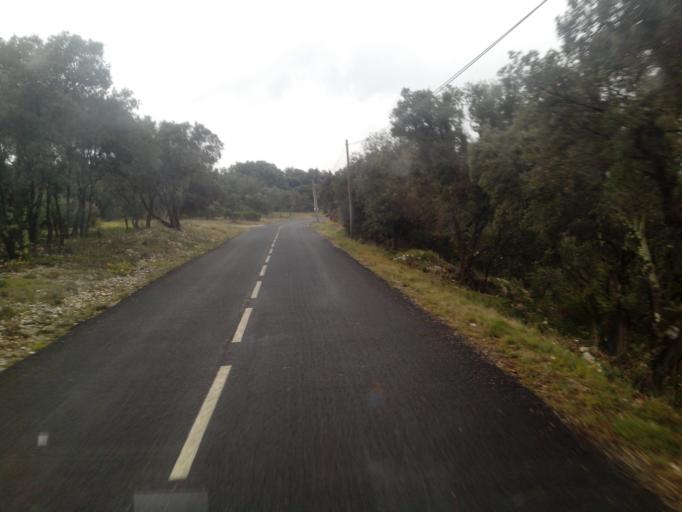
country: FR
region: Languedoc-Roussillon
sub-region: Departement de l'Herault
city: Saint-Martin-de-Londres
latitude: 43.8025
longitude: 3.6401
